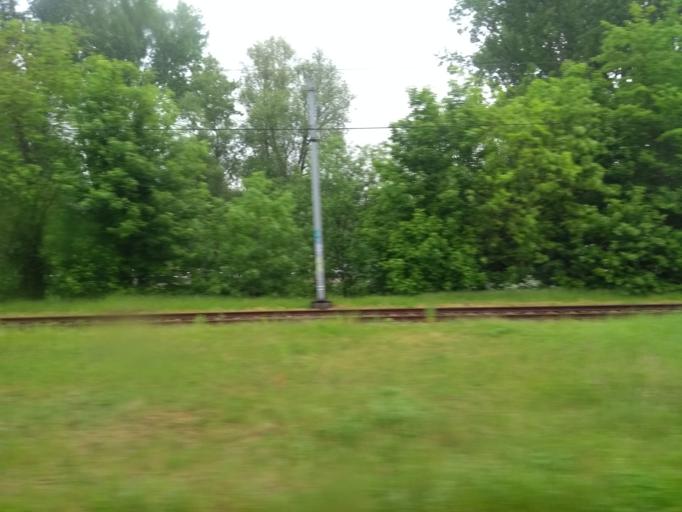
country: NL
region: North Holland
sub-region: Gemeente Haarlem
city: Haarlem
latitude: 52.3863
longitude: 4.6455
